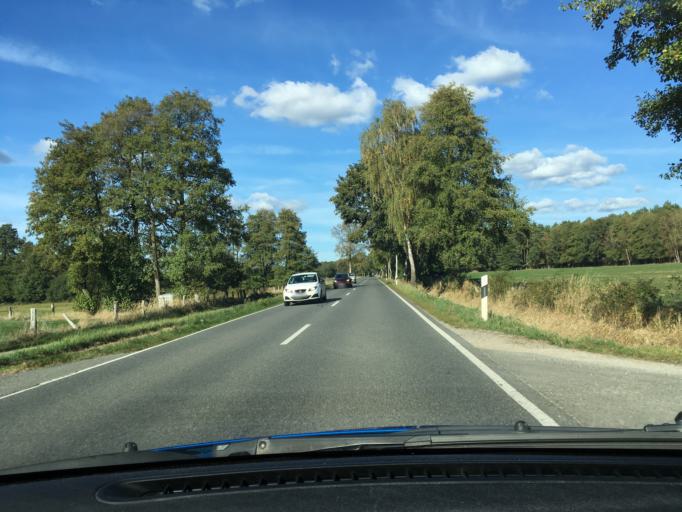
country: DE
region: Lower Saxony
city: Isernhagen Farster Bauerschaft
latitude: 52.5259
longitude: 9.8581
